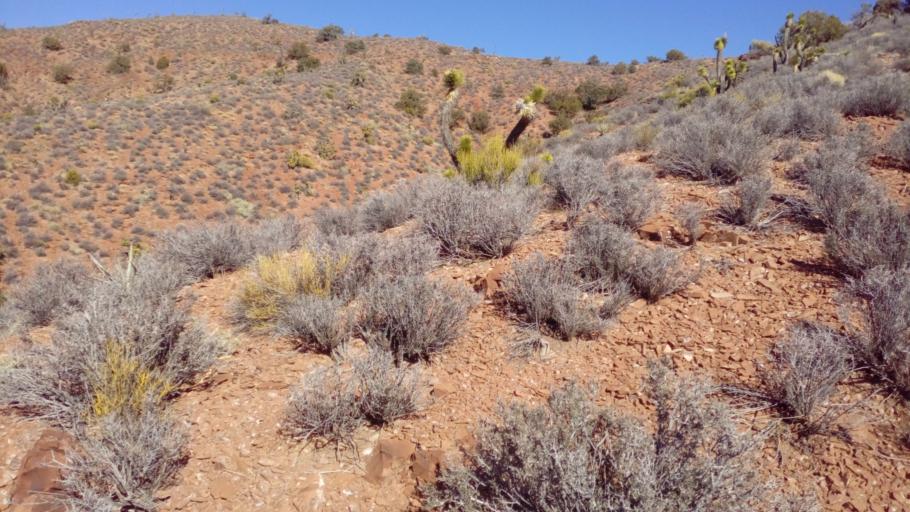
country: US
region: Nevada
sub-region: Clark County
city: Summerlin South
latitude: 36.0614
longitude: -115.5723
